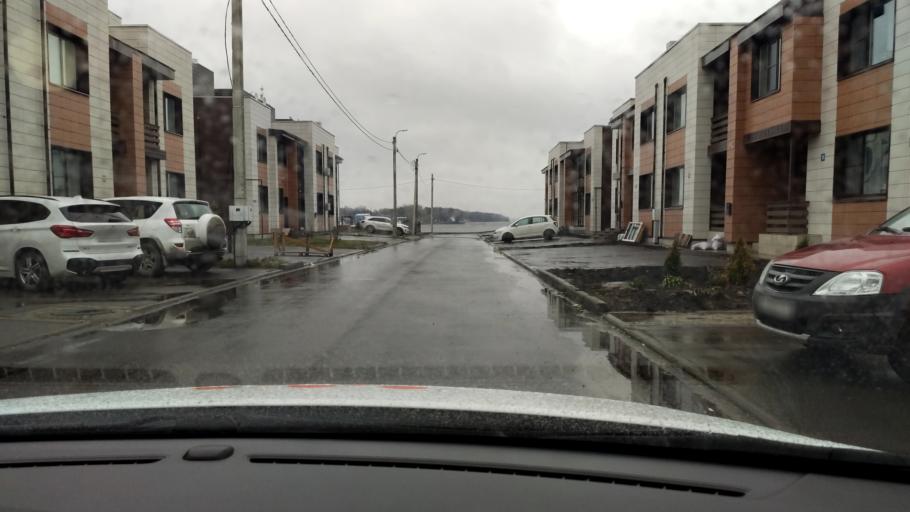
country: RU
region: Tatarstan
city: Staroye Arakchino
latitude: 55.7996
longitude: 48.9654
